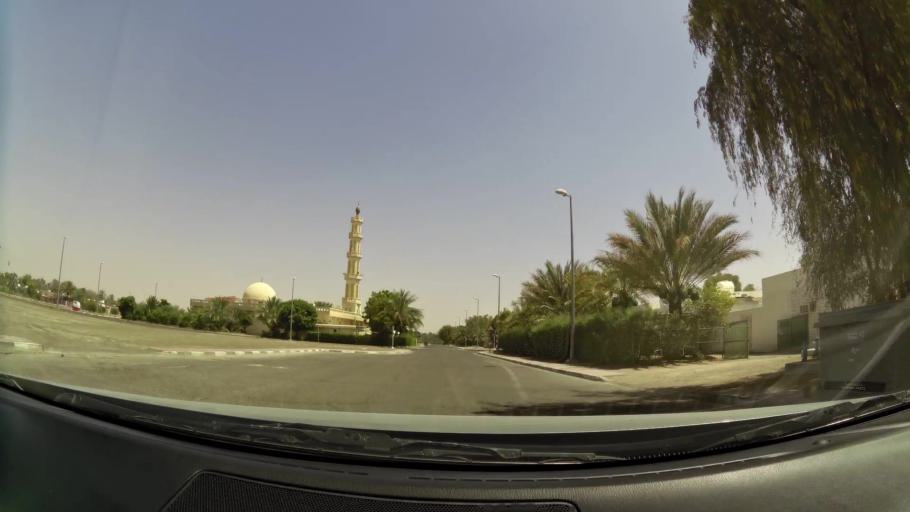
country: OM
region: Al Buraimi
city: Al Buraymi
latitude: 24.2751
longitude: 55.7716
